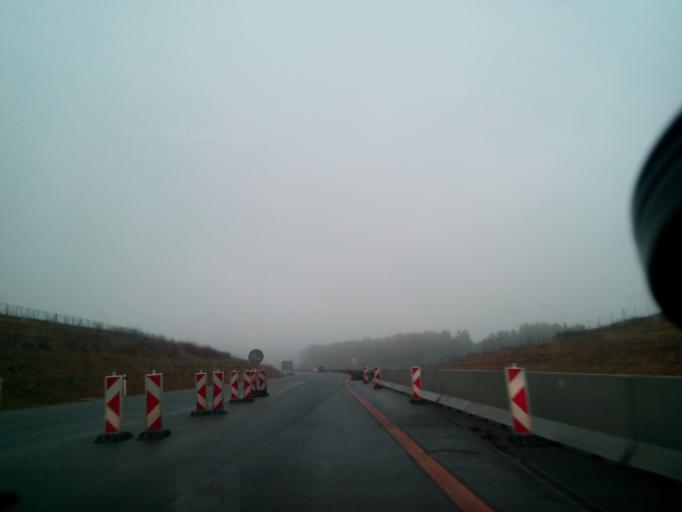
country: SK
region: Presovsky
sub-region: Okres Presov
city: Presov
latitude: 48.9987
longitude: 21.1908
